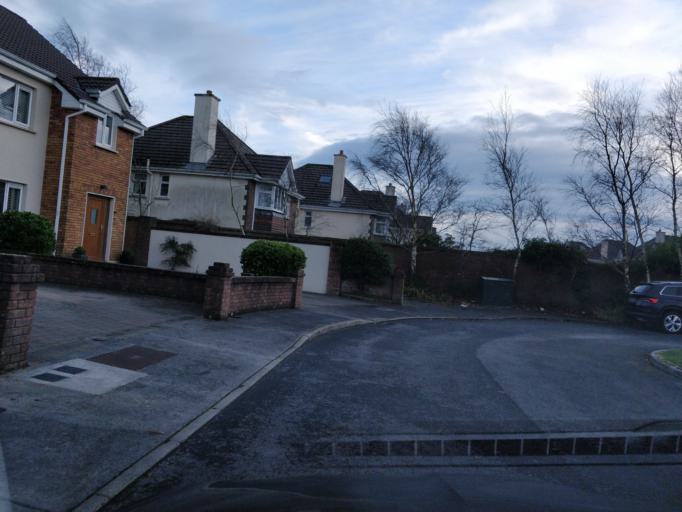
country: IE
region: Connaught
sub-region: County Galway
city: Bearna
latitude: 53.2677
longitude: -9.1088
